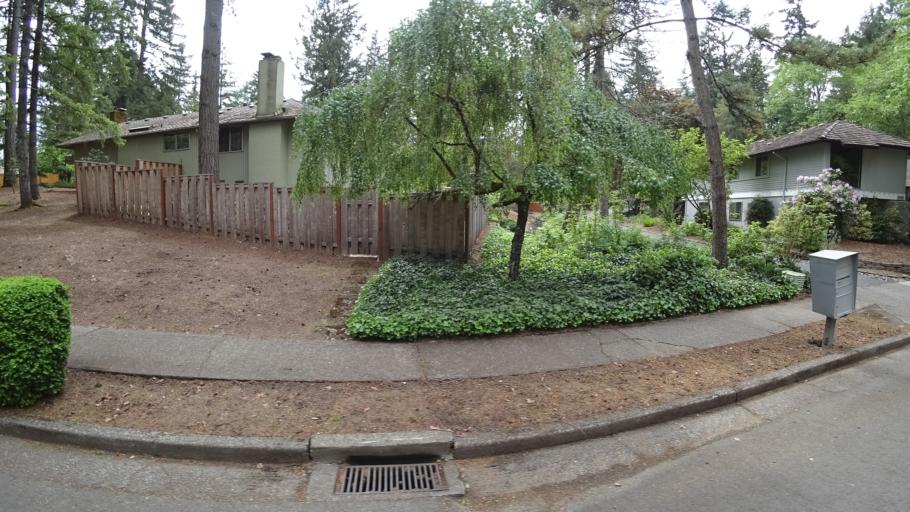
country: US
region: Oregon
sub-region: Washington County
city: Beaverton
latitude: 45.4782
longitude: -122.8330
